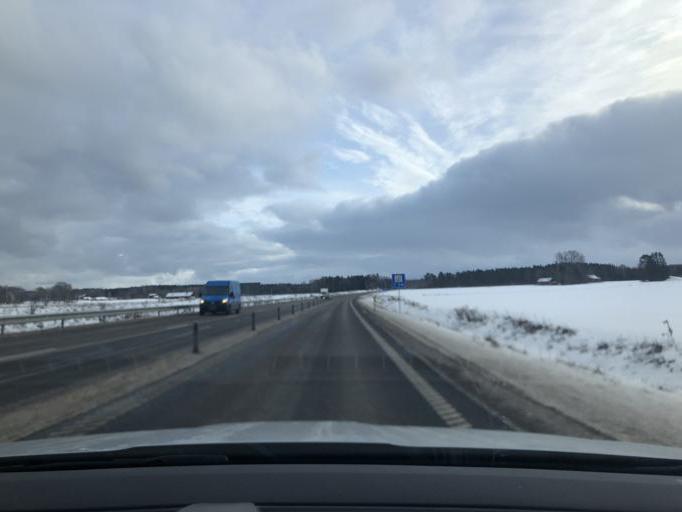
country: SE
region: OEstergoetland
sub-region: Motala Kommun
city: Borensberg
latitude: 58.5798
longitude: 15.2264
